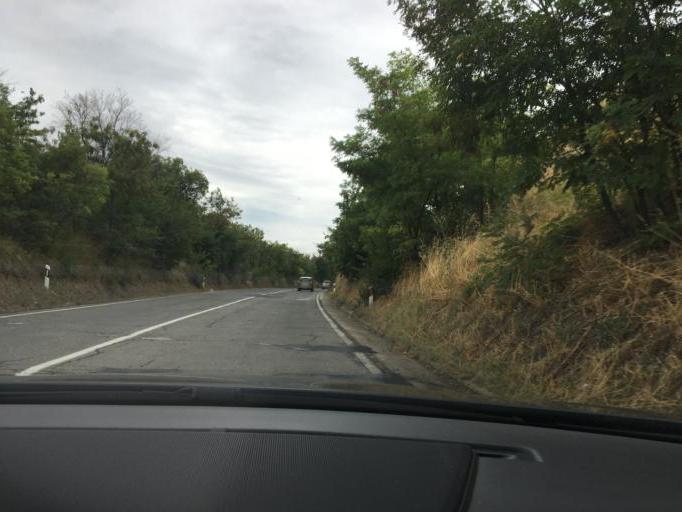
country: MK
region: Staro Nagoricane
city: Staro Nagorichane
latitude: 42.1704
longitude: 21.7730
